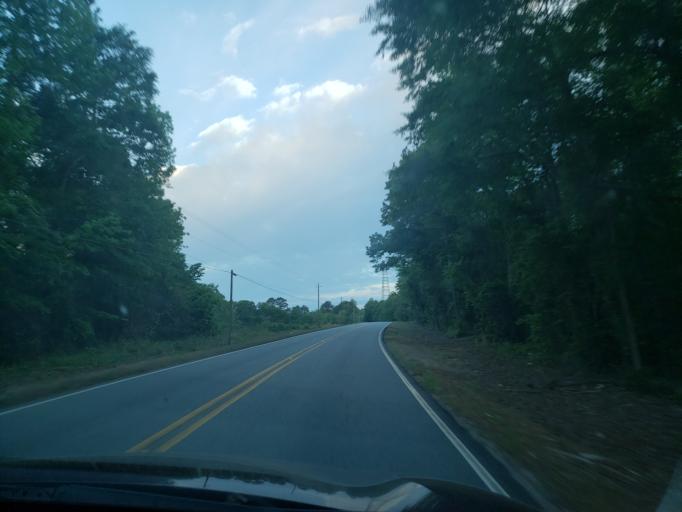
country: US
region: Alabama
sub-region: Tallapoosa County
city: Camp Hill
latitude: 32.6982
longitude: -85.6759
